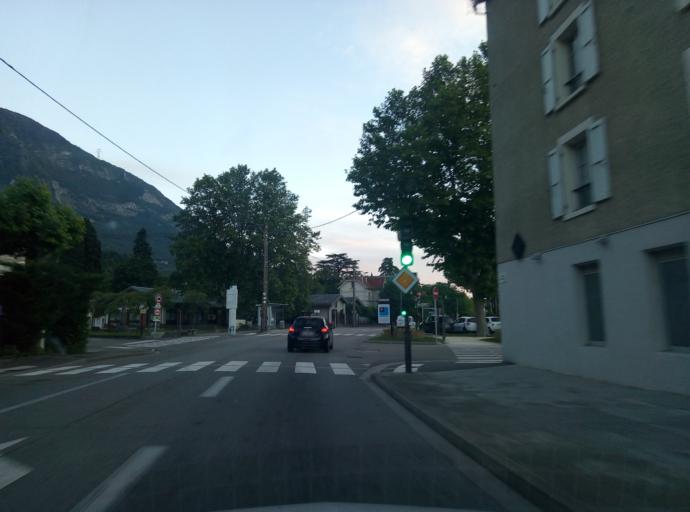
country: FR
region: Rhone-Alpes
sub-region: Departement de l'Isere
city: Sassenage
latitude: 45.2063
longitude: 5.6631
